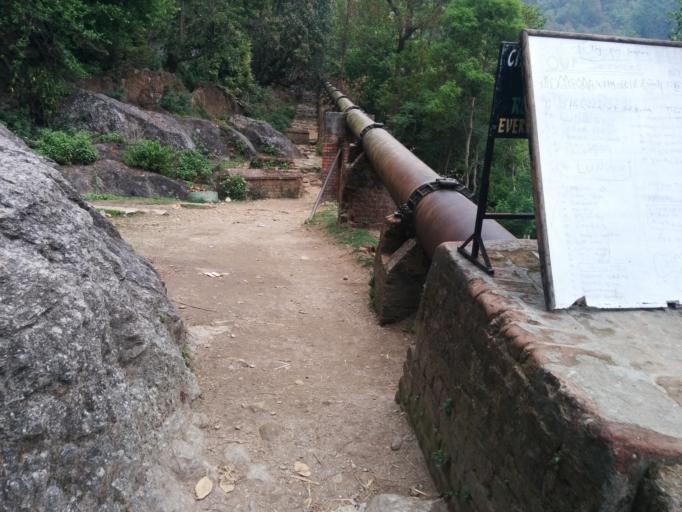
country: NP
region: Central Region
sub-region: Bagmati Zone
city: Bhaktapur
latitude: 27.7642
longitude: 85.4232
